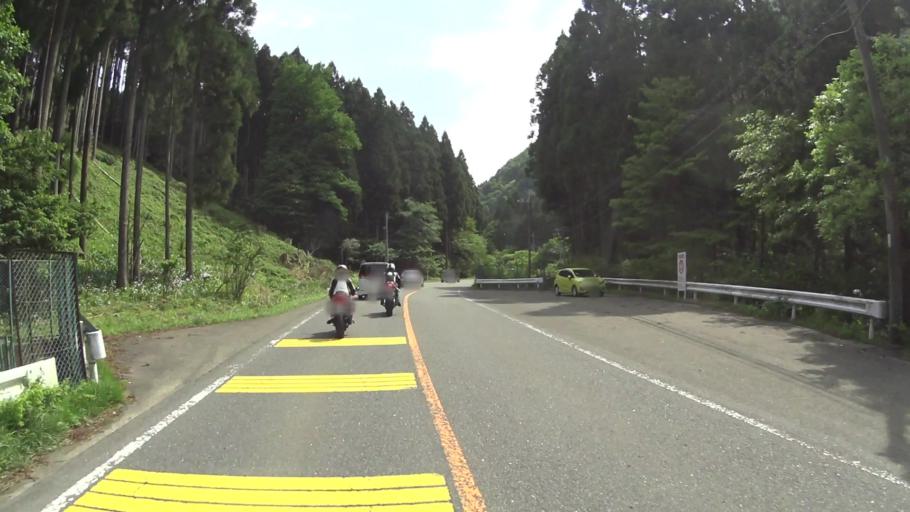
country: JP
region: Shiga Prefecture
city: Kitahama
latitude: 35.2780
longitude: 135.8795
